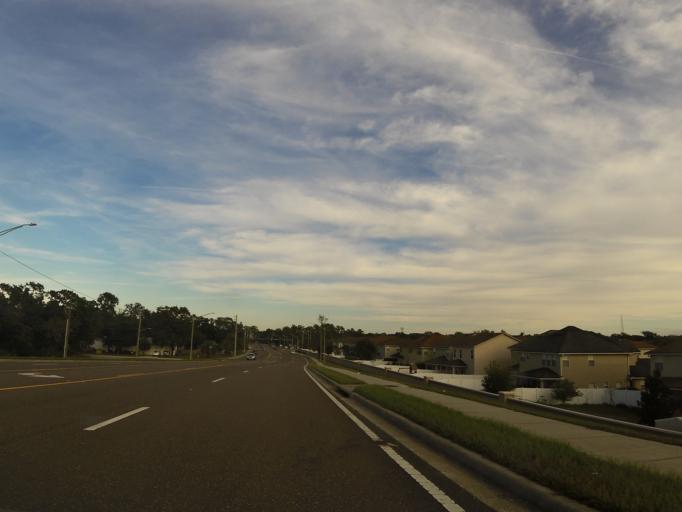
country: US
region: Florida
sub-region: Saint Johns County
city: Fruit Cove
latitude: 30.1619
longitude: -81.5514
